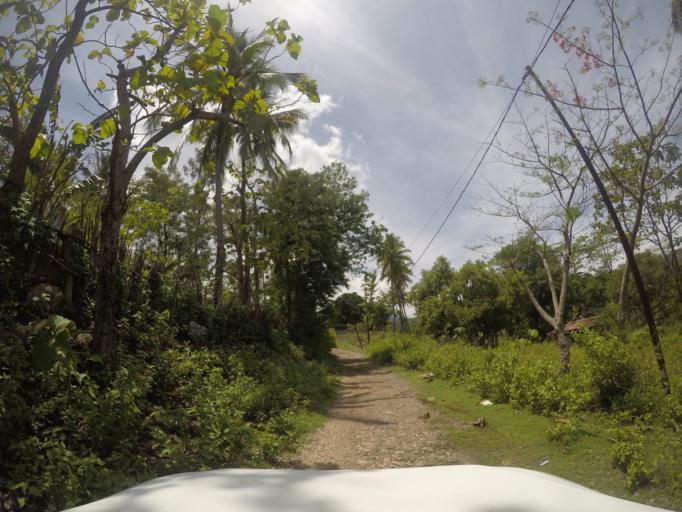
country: TL
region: Bobonaro
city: Maliana
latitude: -8.9991
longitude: 125.2249
